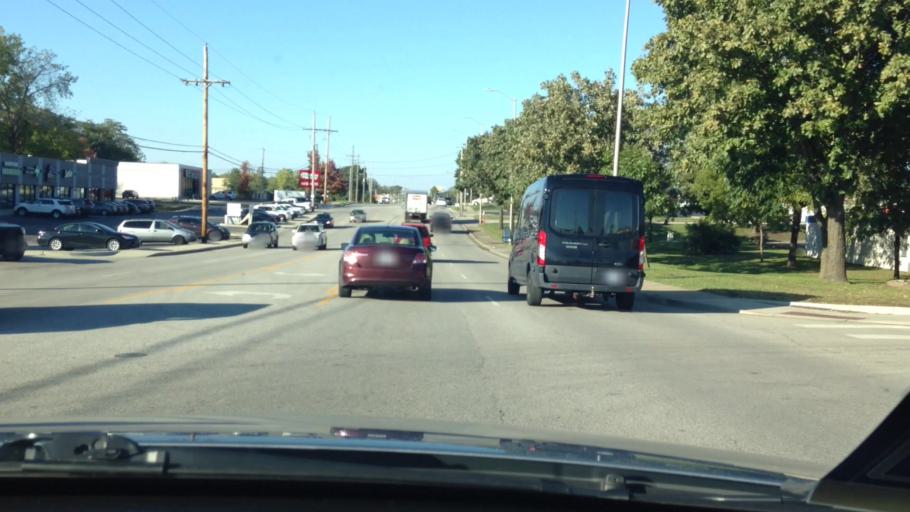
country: US
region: Missouri
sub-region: Clay County
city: Gladstone
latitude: 39.2327
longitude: -94.5761
